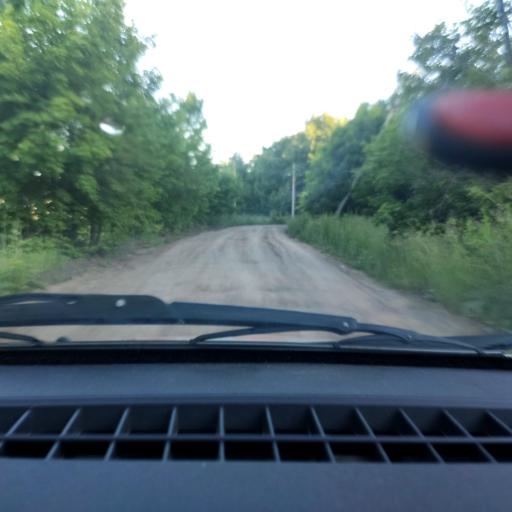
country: RU
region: Bashkortostan
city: Karmaskaly
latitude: 54.3711
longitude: 55.9108
